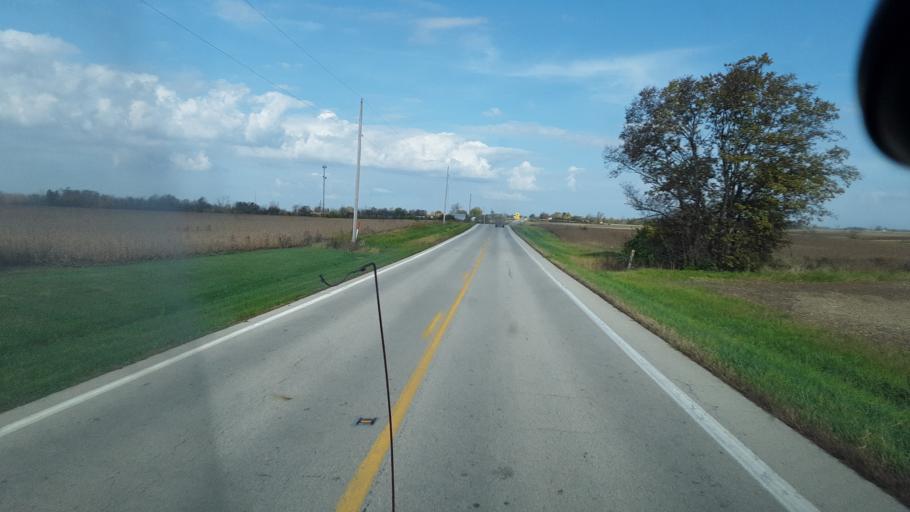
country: US
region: Ohio
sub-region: Clinton County
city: Sabina
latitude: 39.5469
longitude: -83.7126
